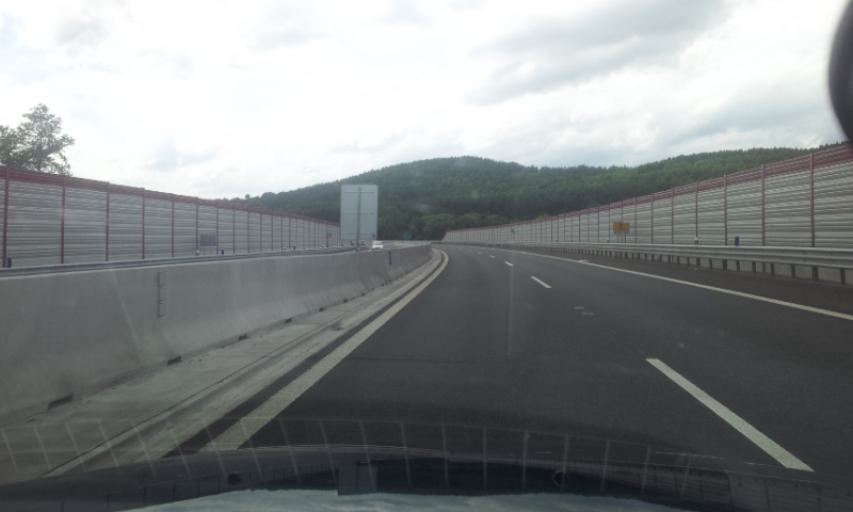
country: SK
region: Banskobystricky
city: Detva
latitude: 48.5366
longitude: 19.4473
